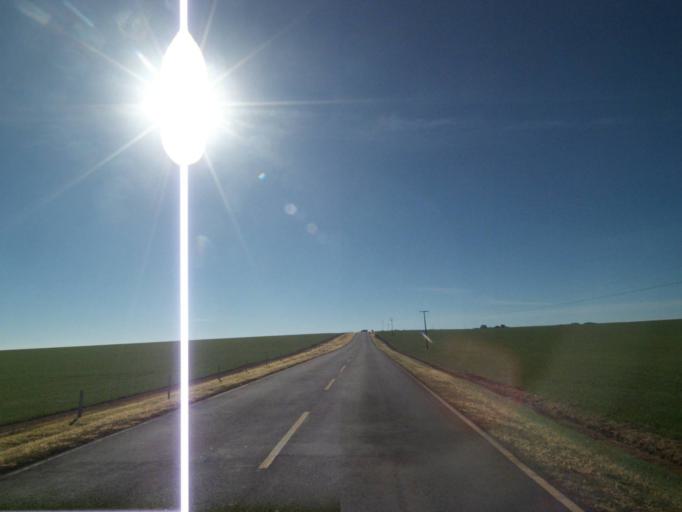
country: BR
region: Parana
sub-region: Tibagi
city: Tibagi
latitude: -24.5214
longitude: -50.3530
